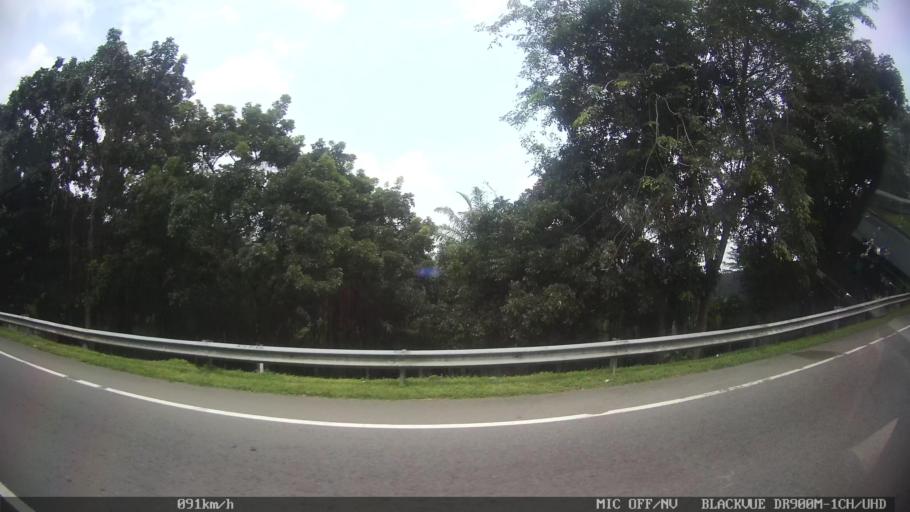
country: ID
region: North Sumatra
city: Labuhan Deli
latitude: 3.6854
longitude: 98.6814
